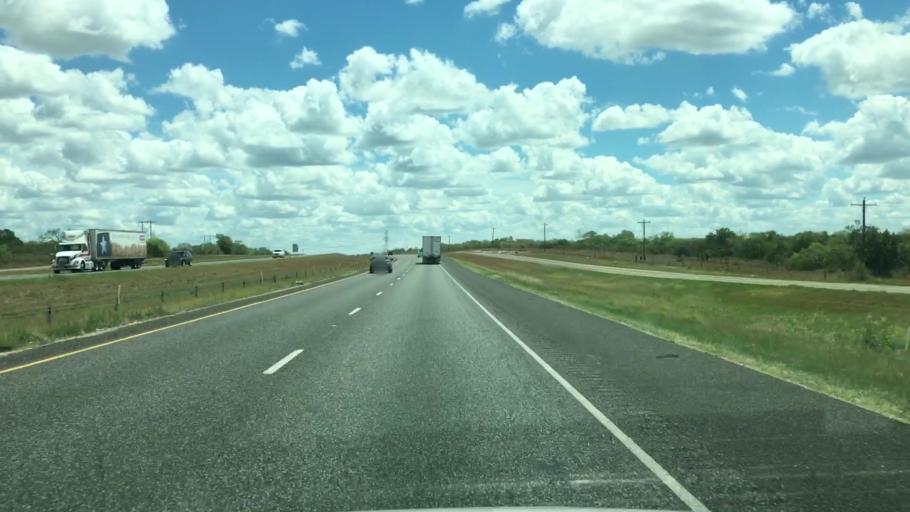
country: US
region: Texas
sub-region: Atascosa County
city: Pleasanton
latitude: 28.8310
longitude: -98.3694
